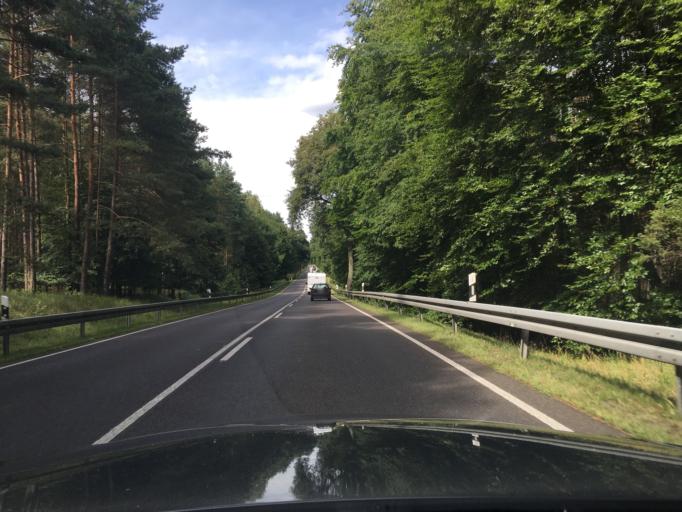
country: DE
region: Brandenburg
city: Furstenberg
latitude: 53.2649
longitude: 13.1161
